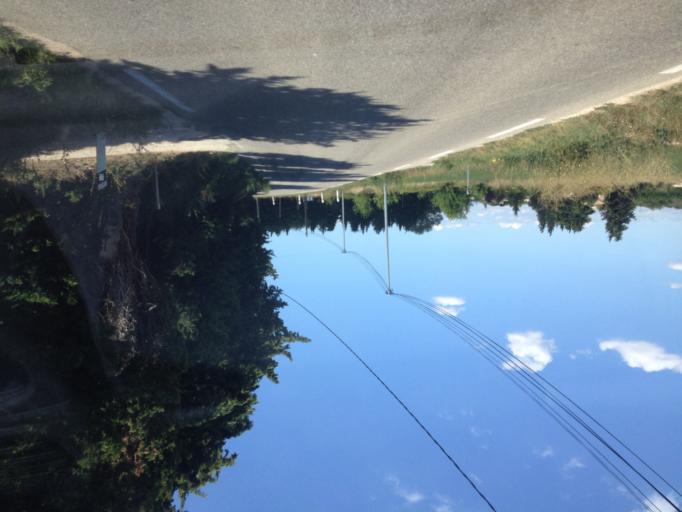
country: FR
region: Provence-Alpes-Cote d'Azur
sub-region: Departement du Vaucluse
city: Orange
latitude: 44.0968
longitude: 4.8014
